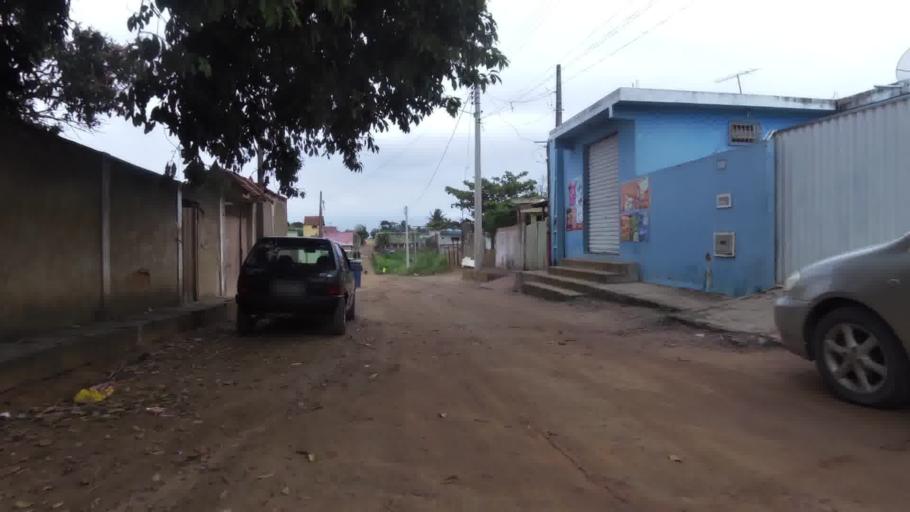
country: BR
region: Espirito Santo
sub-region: Marataizes
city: Marataizes
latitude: -21.0490
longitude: -40.8361
